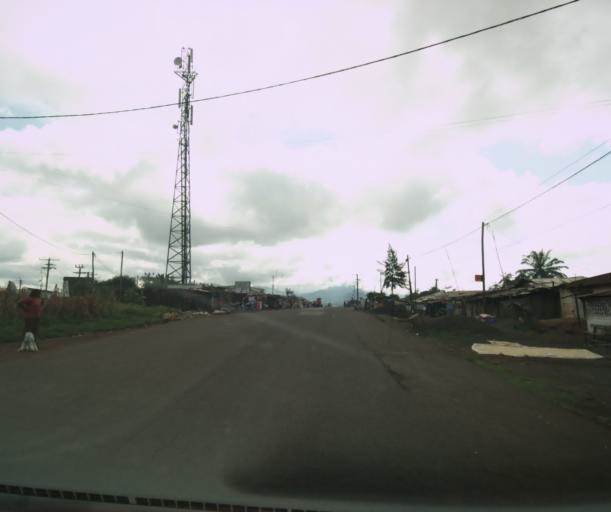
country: CM
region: West
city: Foumbot
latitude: 5.5056
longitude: 10.6233
